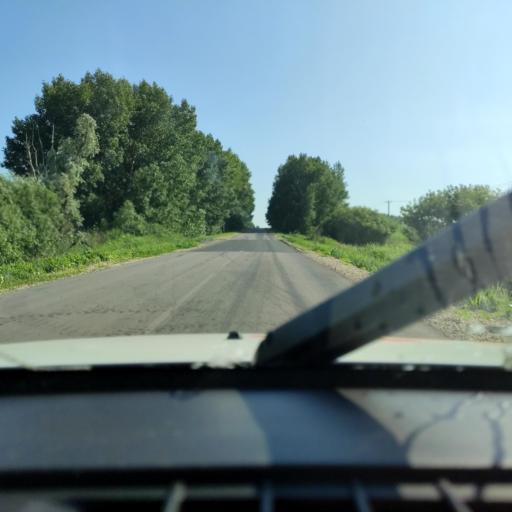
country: RU
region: Voronezj
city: Anna
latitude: 51.6373
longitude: 40.3593
